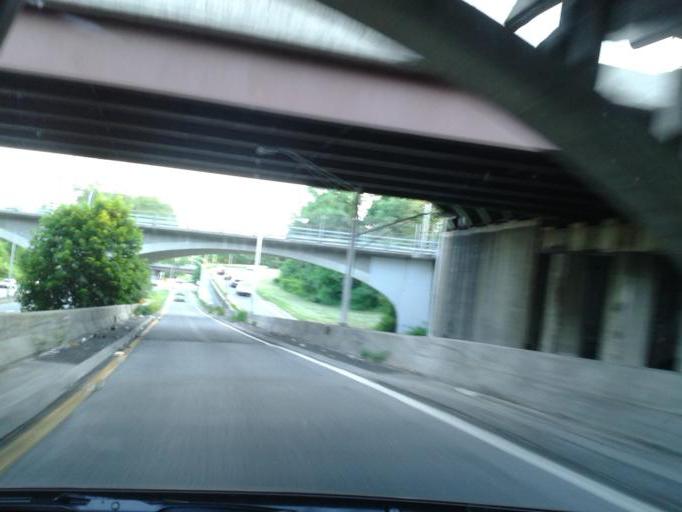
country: US
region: New York
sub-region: Westchester County
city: Bronxville
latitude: 40.9283
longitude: -73.8404
